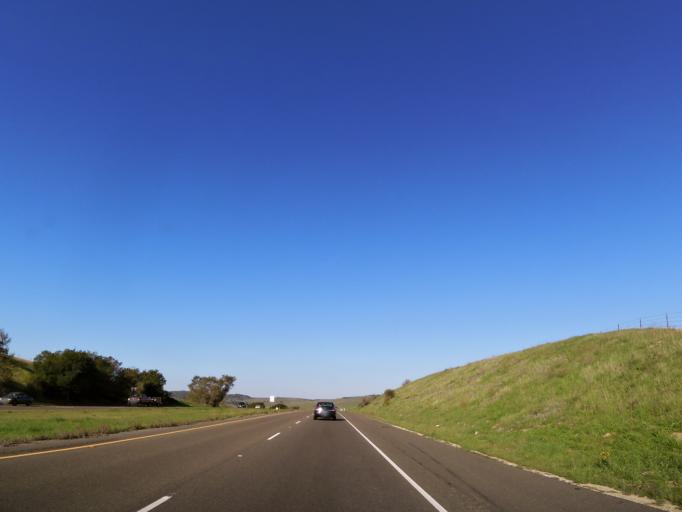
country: US
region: California
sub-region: Santa Barbara County
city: Los Alamos
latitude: 34.7893
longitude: -120.3281
